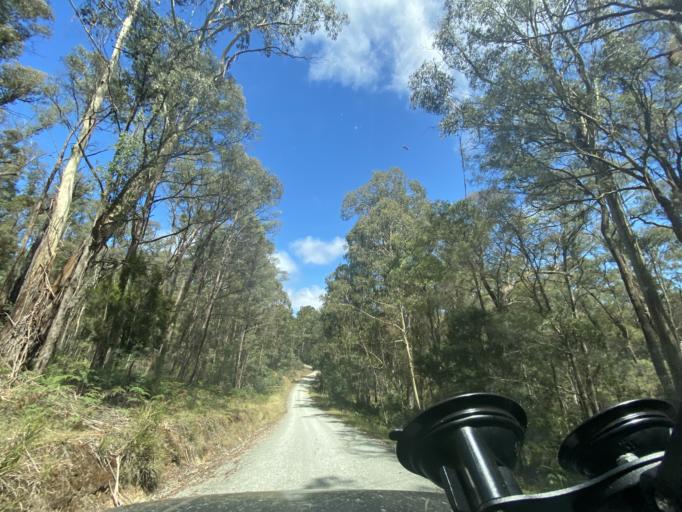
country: AU
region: Victoria
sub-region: Yarra Ranges
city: Millgrove
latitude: -37.5190
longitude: 146.0280
